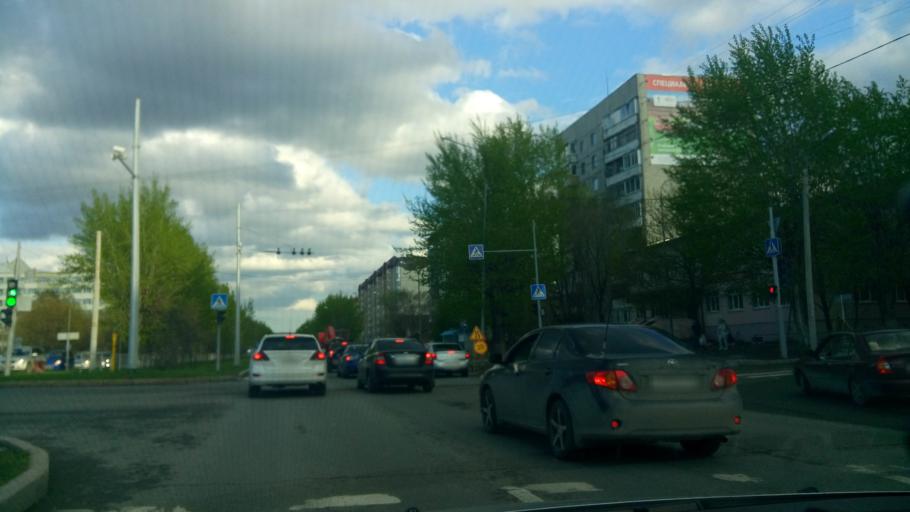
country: RU
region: Tjumen
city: Tyumen
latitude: 57.1385
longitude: 65.5949
